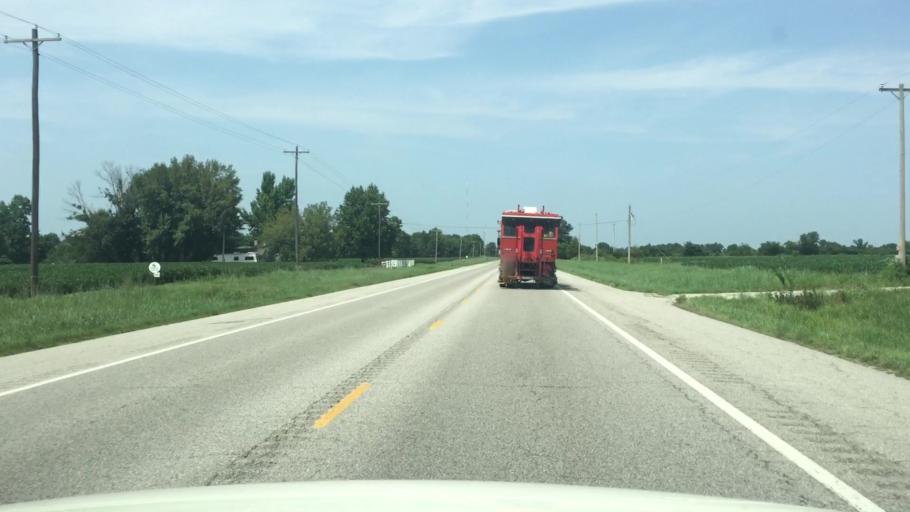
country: US
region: Kansas
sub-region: Cherokee County
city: Galena
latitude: 37.1864
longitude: -94.7045
